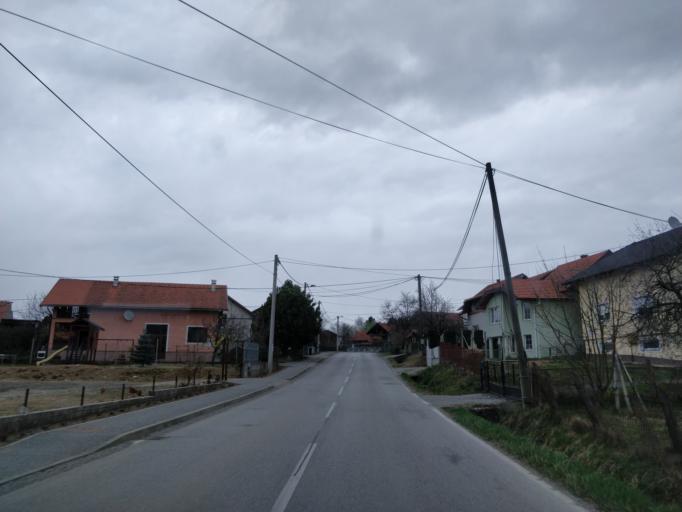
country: HR
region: Zagrebacka
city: Jakovlje
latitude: 45.9168
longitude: 15.8915
